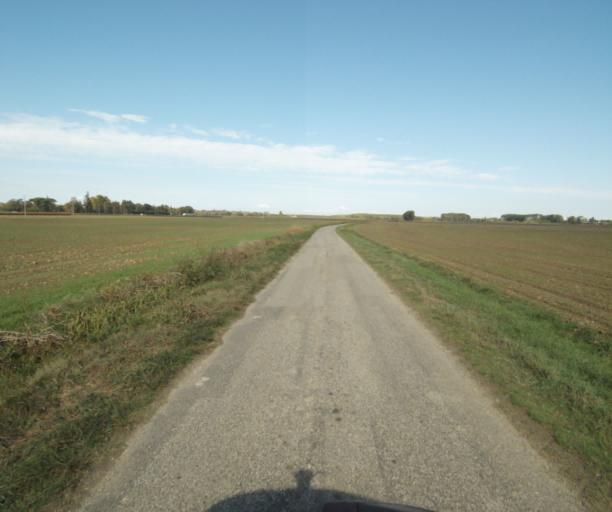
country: FR
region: Midi-Pyrenees
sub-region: Departement du Tarn-et-Garonne
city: Finhan
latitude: 43.8857
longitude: 1.2213
